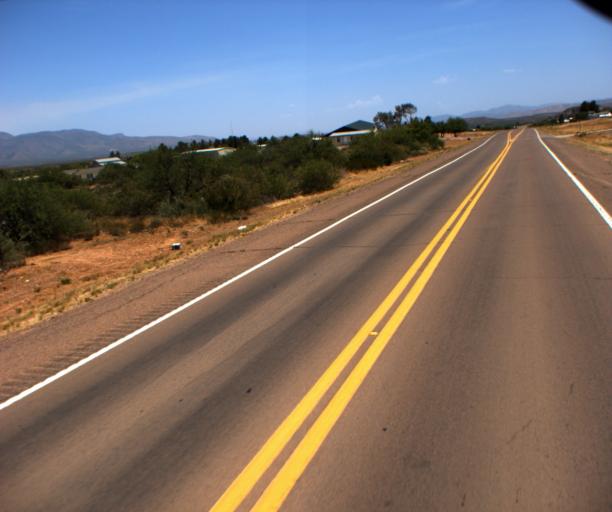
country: US
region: Arizona
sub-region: Gila County
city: Tonto Basin
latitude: 33.8474
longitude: -111.3087
